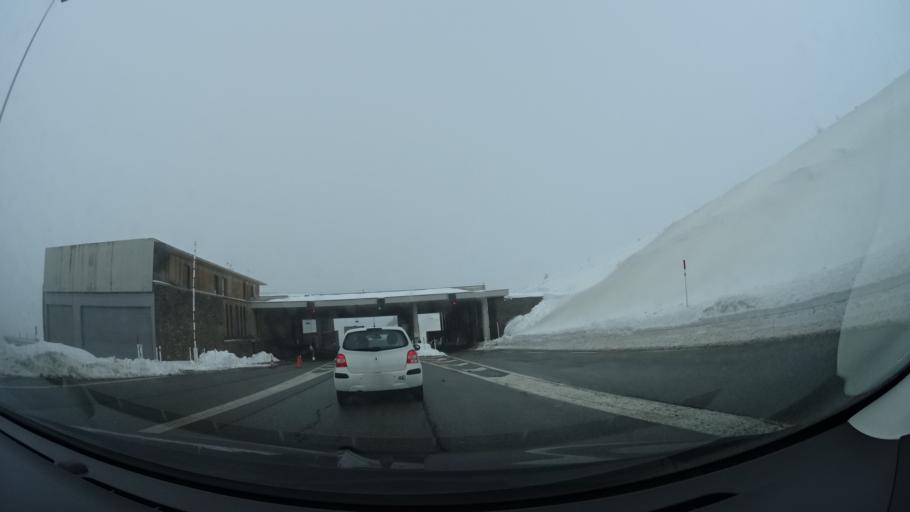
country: AD
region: Encamp
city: Pas de la Casa
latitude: 42.5591
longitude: 1.7557
